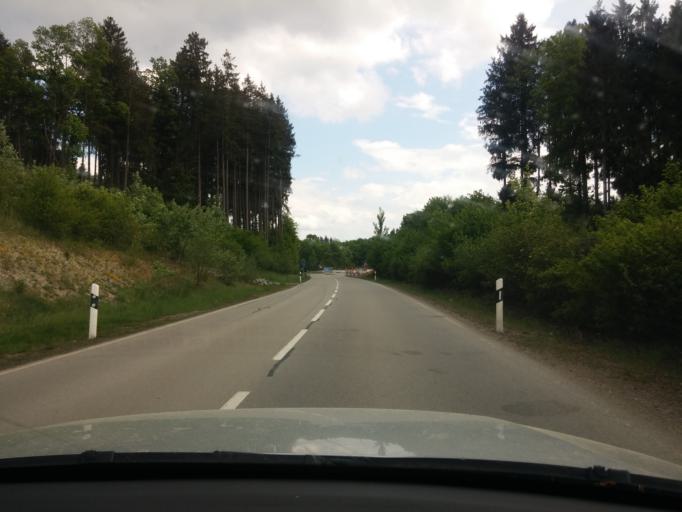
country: DE
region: Bavaria
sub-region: Upper Bavaria
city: Holzkirchen
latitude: 47.8855
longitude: 11.7156
